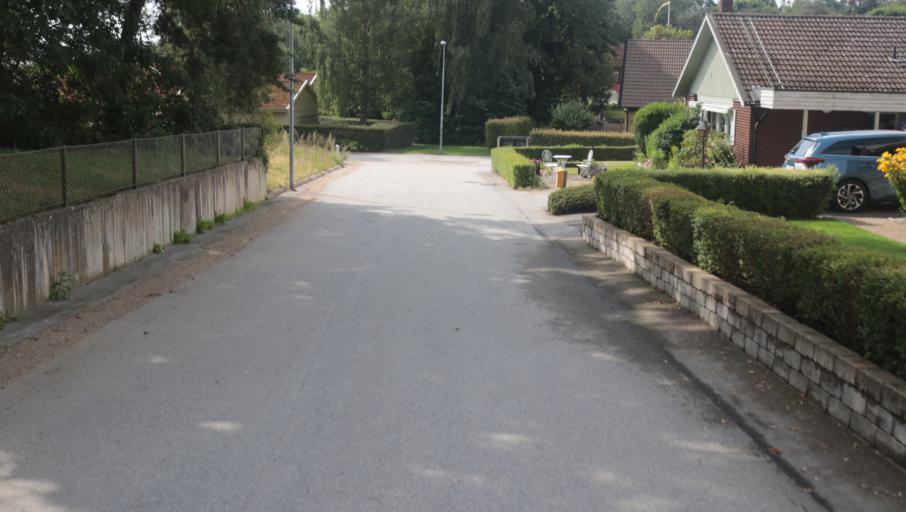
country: SE
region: Blekinge
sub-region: Karlshamns Kommun
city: Karlshamn
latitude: 56.2145
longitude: 14.8423
